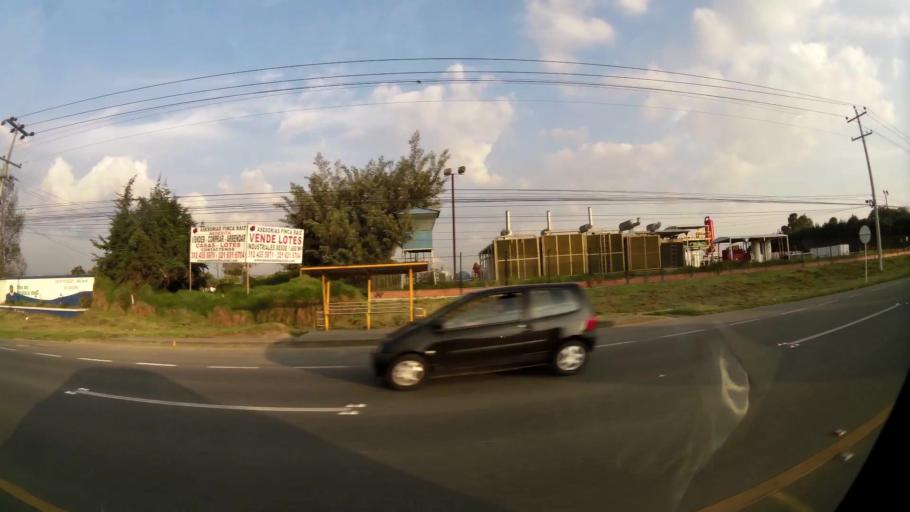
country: CO
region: Cundinamarca
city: Cota
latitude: 4.7719
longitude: -74.1468
